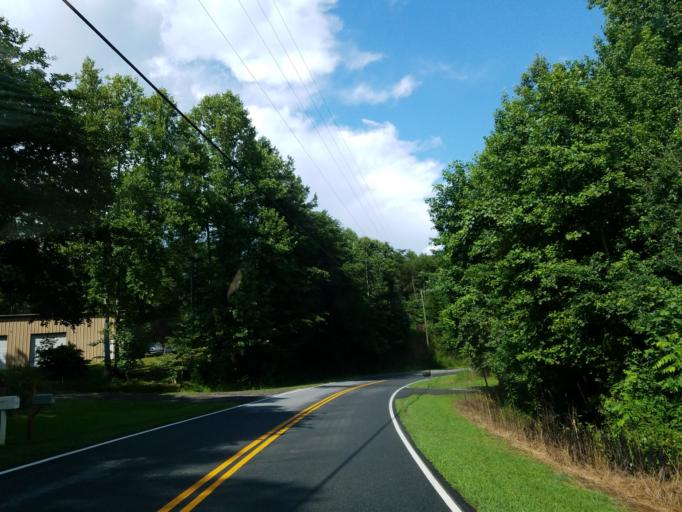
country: US
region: Georgia
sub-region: Gilmer County
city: Ellijay
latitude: 34.6909
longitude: -84.3098
